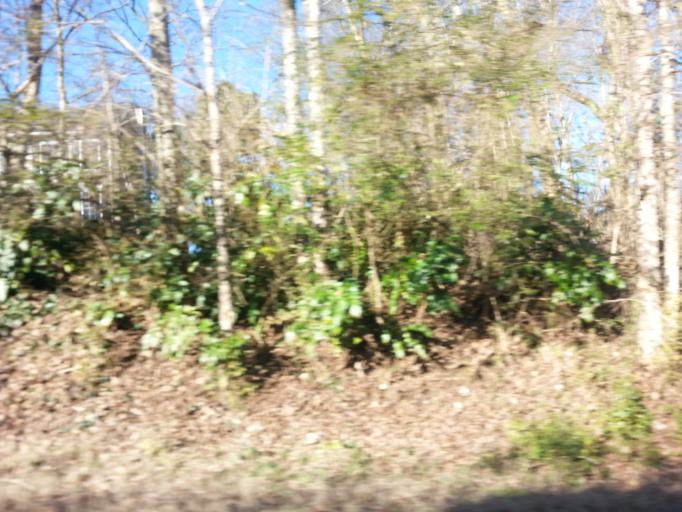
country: US
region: Tennessee
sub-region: Knox County
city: Knoxville
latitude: 35.8902
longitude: -83.9770
